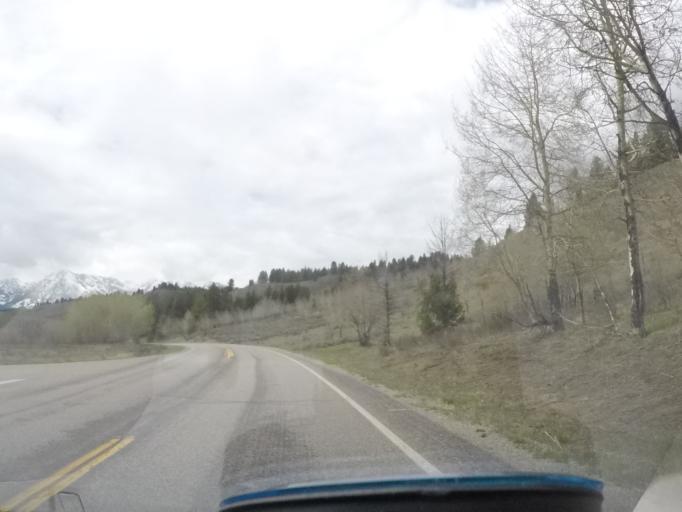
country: US
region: Wyoming
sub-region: Teton County
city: Jackson
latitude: 43.8650
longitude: -110.5392
